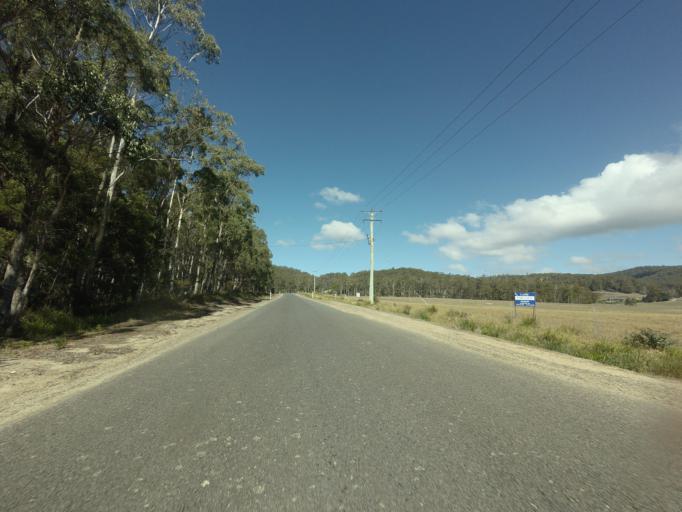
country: AU
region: Tasmania
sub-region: Break O'Day
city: St Helens
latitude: -41.6177
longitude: 148.2162
